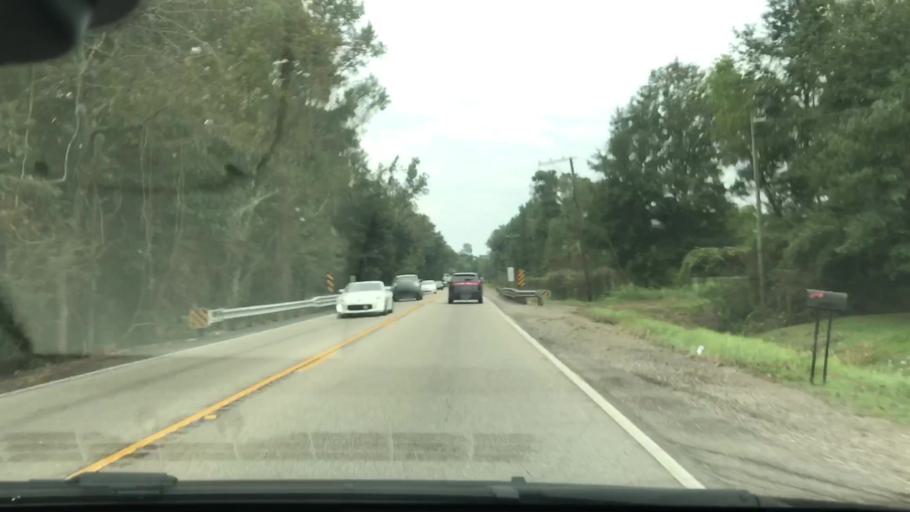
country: US
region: Louisiana
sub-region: Saint Tammany Parish
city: Slidell
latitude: 30.3001
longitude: -89.7746
